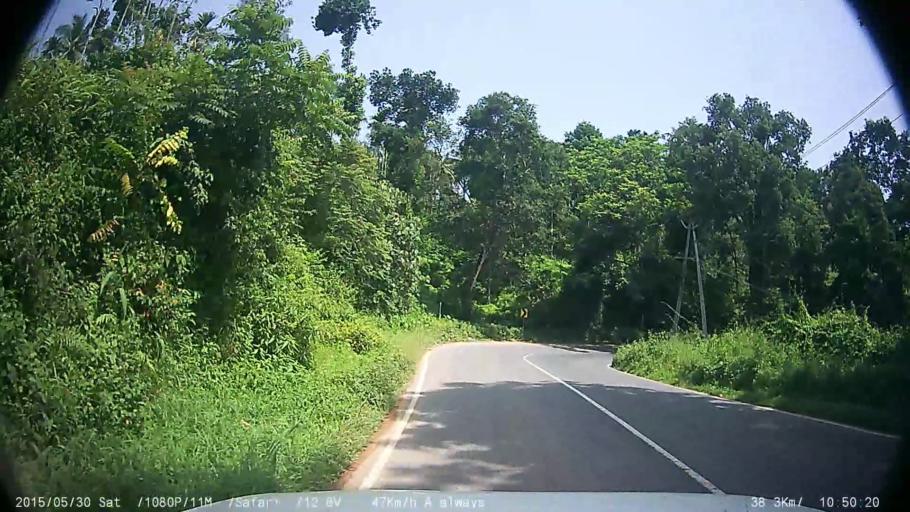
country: IN
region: Kerala
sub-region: Wayanad
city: Kalpetta
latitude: 11.6433
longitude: 76.0870
